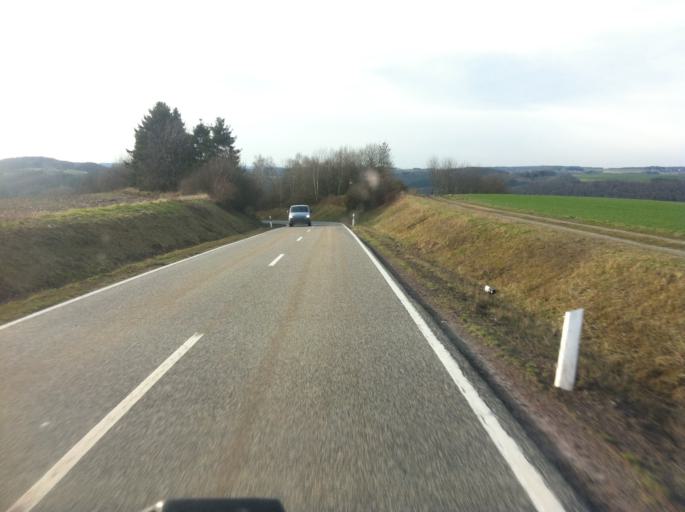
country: DE
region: Rheinland-Pfalz
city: Altlay
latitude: 49.9829
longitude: 7.2793
